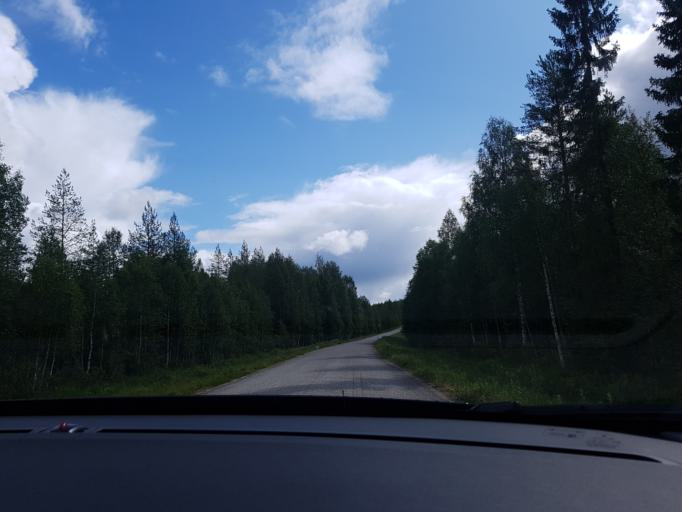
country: FI
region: Kainuu
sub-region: Kehys-Kainuu
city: Kuhmo
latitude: 64.4502
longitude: 29.6826
